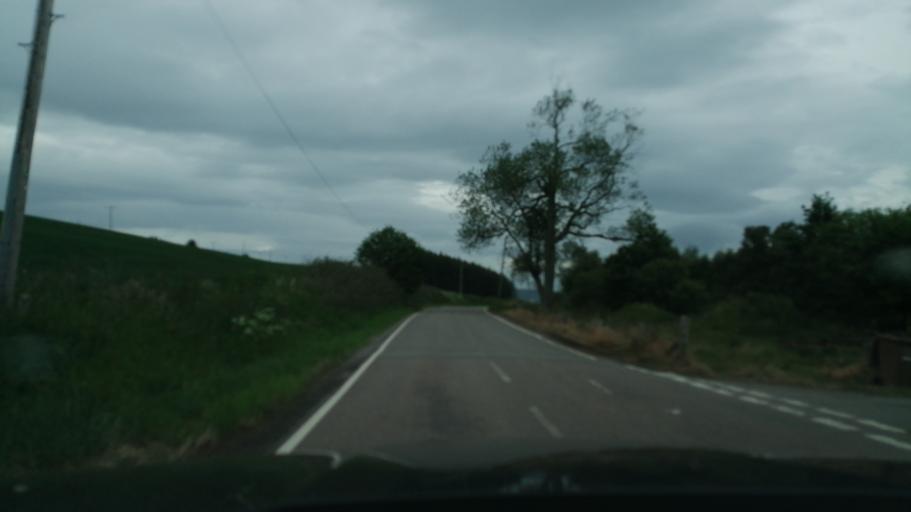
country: GB
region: Scotland
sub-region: Moray
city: Cullen
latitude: 57.6032
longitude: -2.8529
